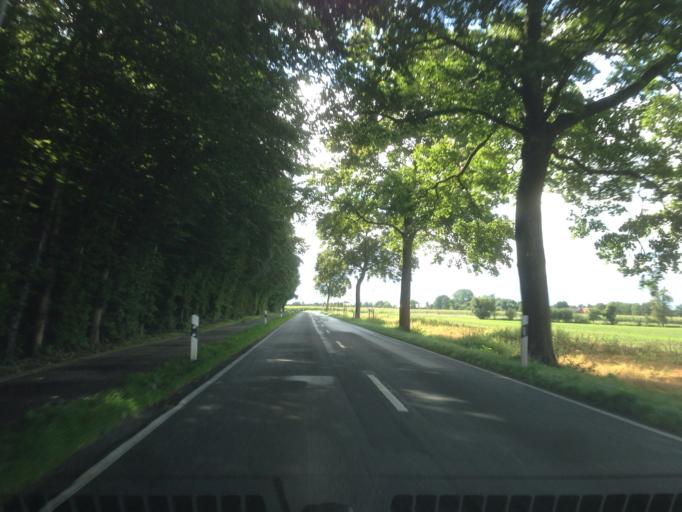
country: DE
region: North Rhine-Westphalia
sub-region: Regierungsbezirk Munster
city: Senden
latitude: 51.8245
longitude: 7.5256
